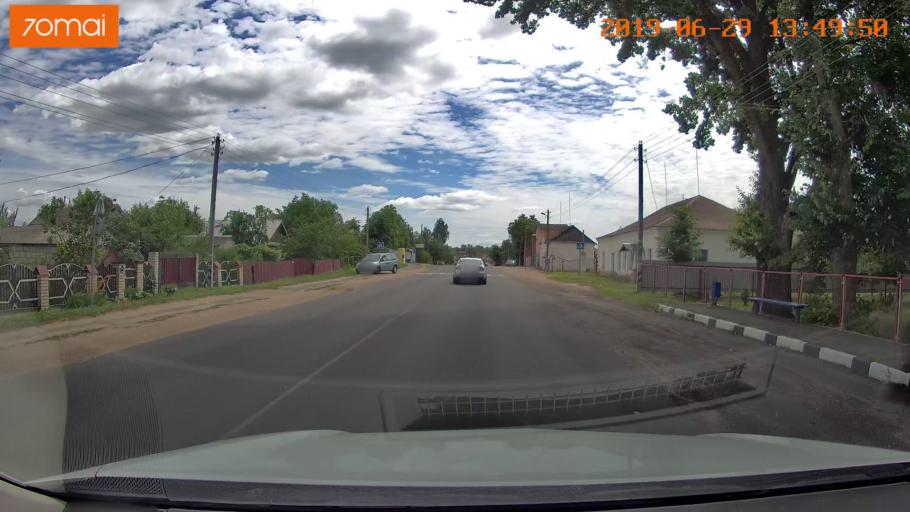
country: BY
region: Minsk
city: Slutsk
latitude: 53.0071
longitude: 27.5656
